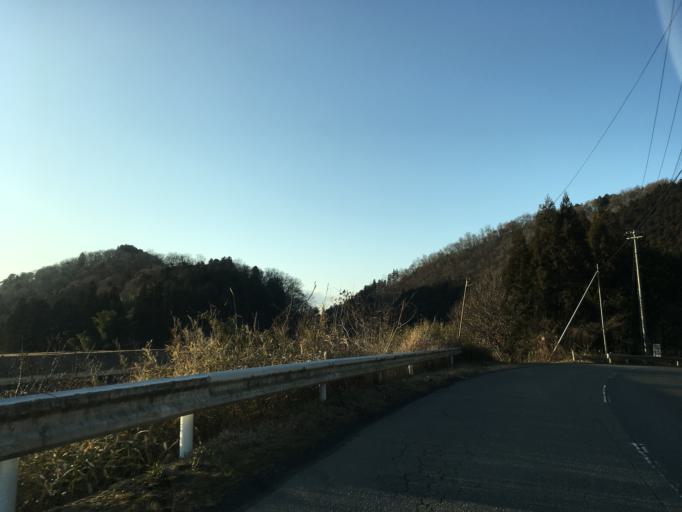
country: JP
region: Iwate
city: Ichinoseki
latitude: 38.8026
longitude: 141.2315
